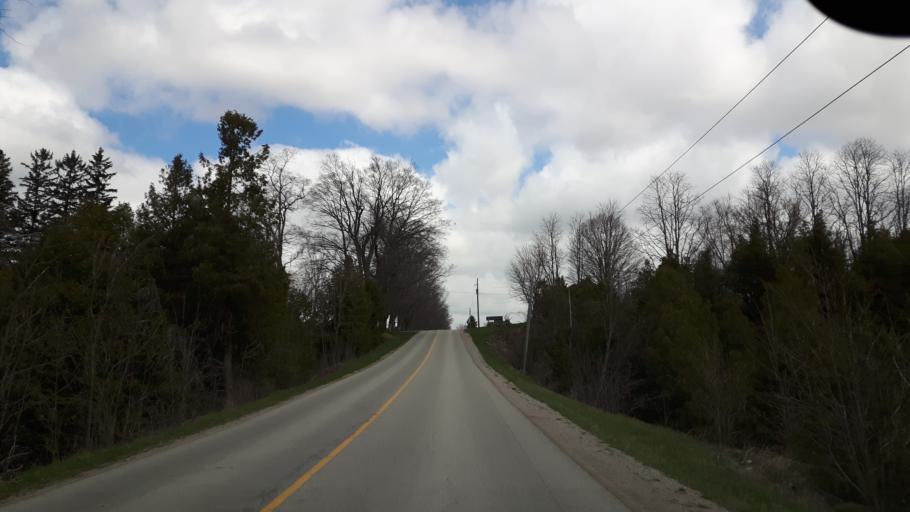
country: CA
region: Ontario
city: Goderich
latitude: 43.6682
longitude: -81.6846
